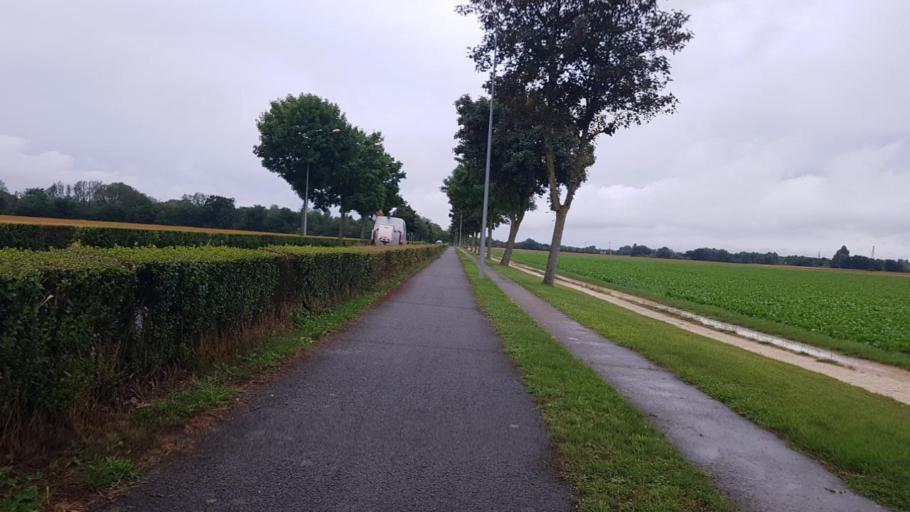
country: FR
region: Champagne-Ardenne
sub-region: Departement de la Marne
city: Sarry
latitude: 48.9250
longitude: 4.3980
